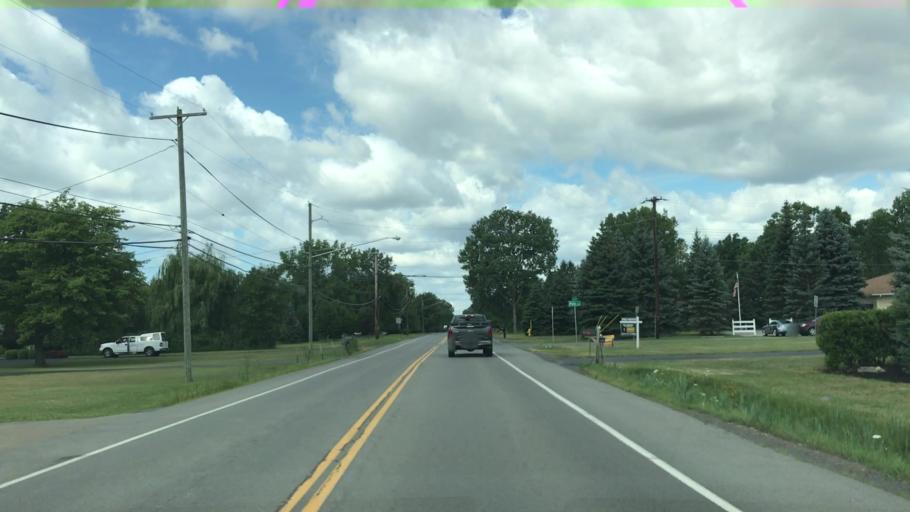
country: US
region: New York
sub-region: Erie County
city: Depew
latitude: 42.8923
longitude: -78.6998
